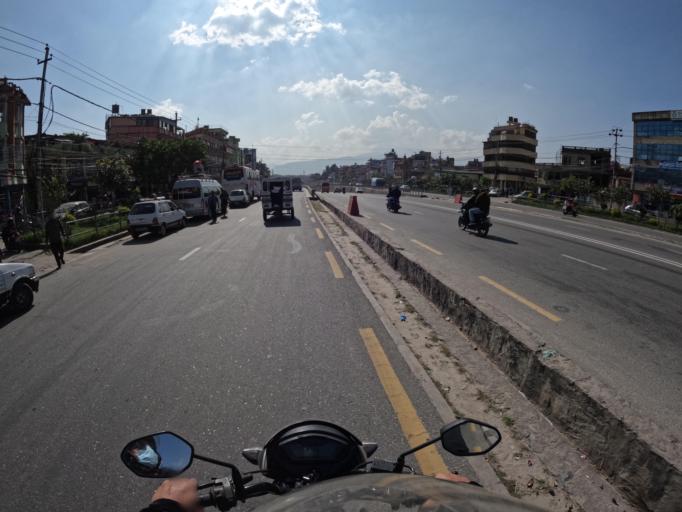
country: NP
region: Central Region
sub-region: Bagmati Zone
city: Patan
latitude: 27.6761
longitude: 85.3455
